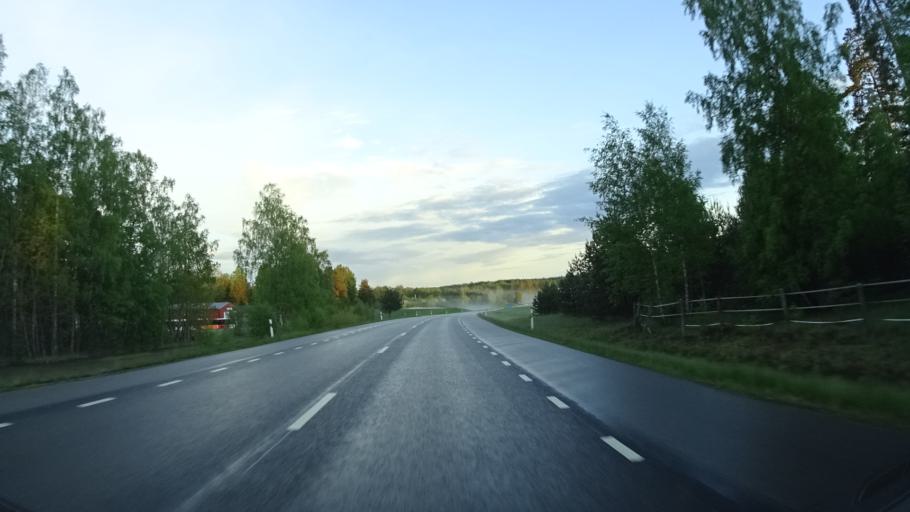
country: SE
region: OEstergoetland
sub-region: Soderkopings Kommun
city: Soederkoeping
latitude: 58.4586
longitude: 16.3650
